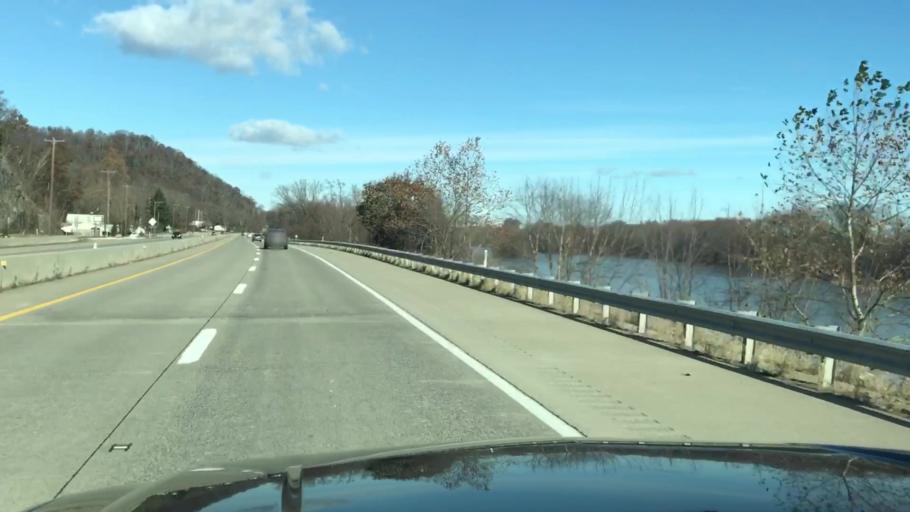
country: US
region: Pennsylvania
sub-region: Dauphin County
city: Millersburg
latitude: 40.6089
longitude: -76.9533
